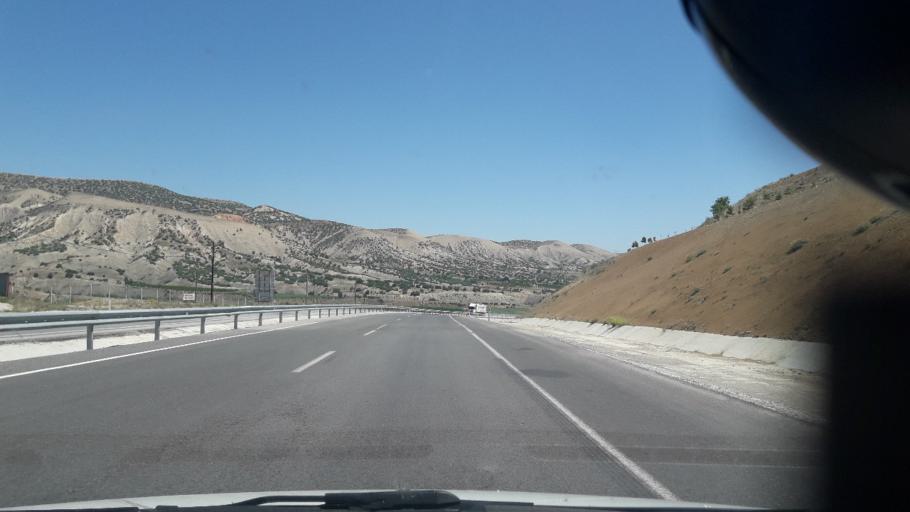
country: TR
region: Malatya
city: Hekimhan
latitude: 38.8074
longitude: 37.9545
